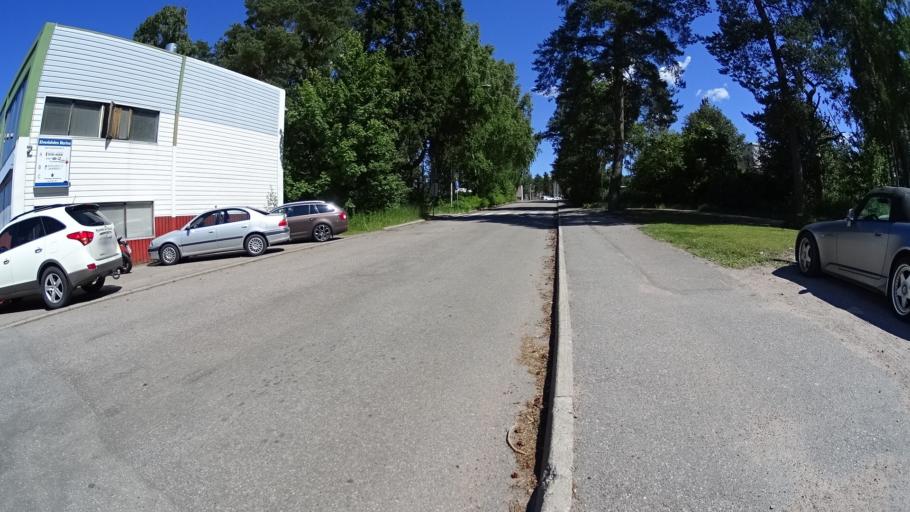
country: FI
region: Uusimaa
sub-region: Helsinki
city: Espoo
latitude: 60.1559
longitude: 24.6246
